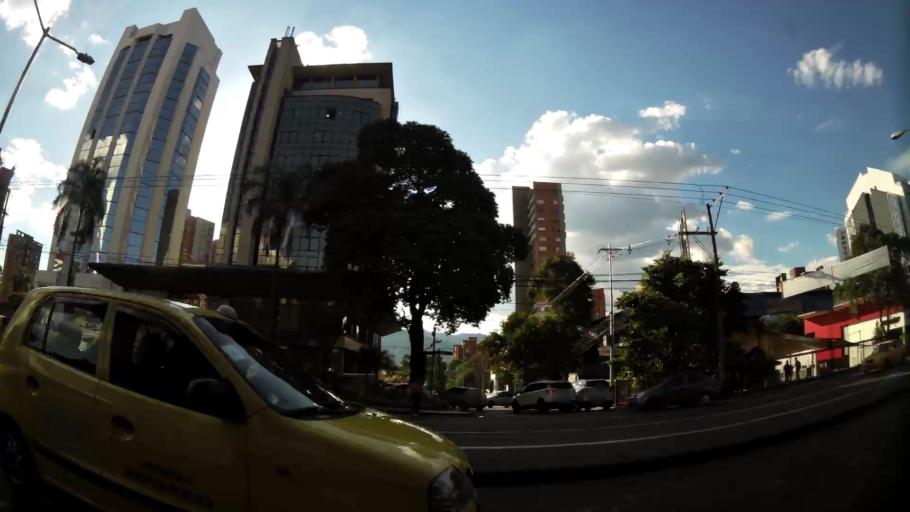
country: CO
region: Antioquia
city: Envigado
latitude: 6.1903
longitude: -75.5769
